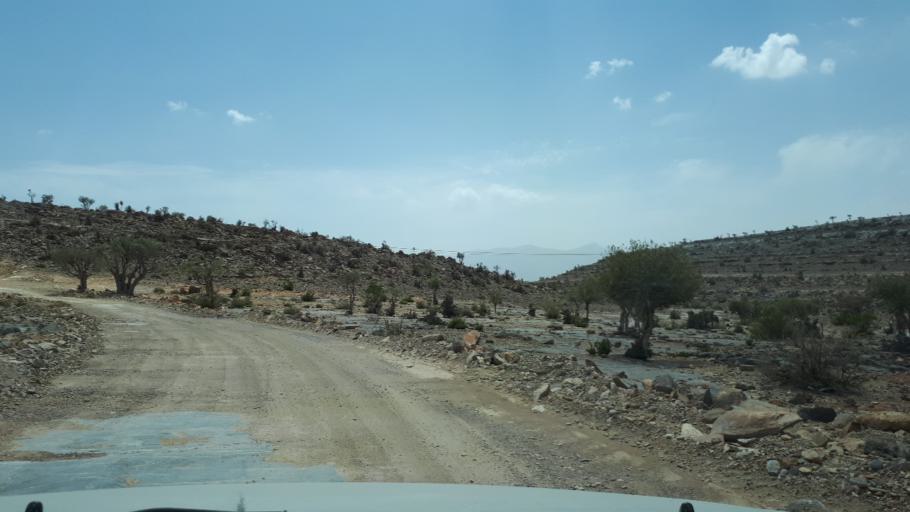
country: OM
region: Muhafazat ad Dakhiliyah
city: Bahla'
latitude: 23.2042
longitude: 57.2011
